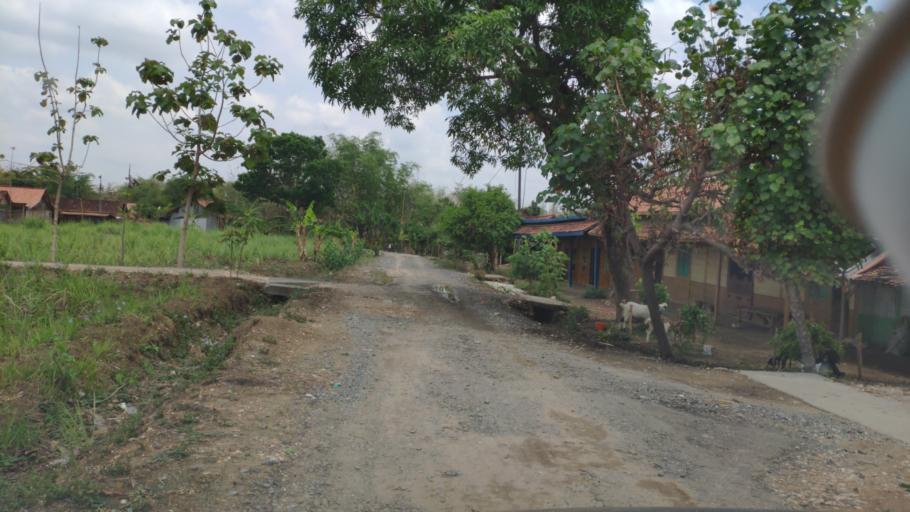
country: ID
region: Central Java
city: Gumiring
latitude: -7.0429
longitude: 111.3919
